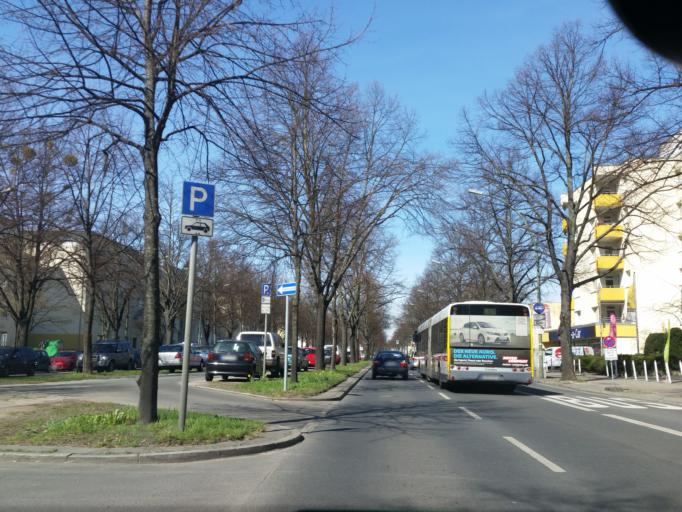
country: DE
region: Berlin
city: Mariendorf
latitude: 52.4323
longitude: 13.3913
